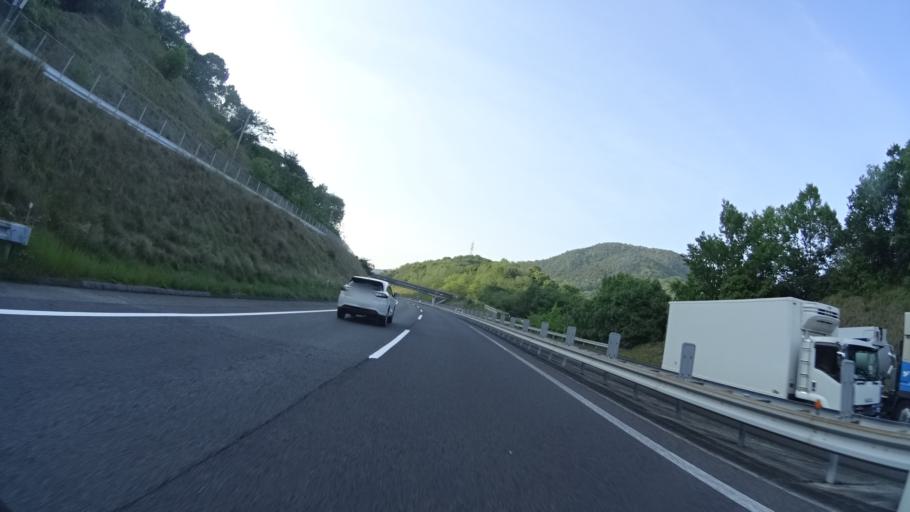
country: JP
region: Kagawa
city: Tadotsu
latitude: 34.2015
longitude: 133.7336
